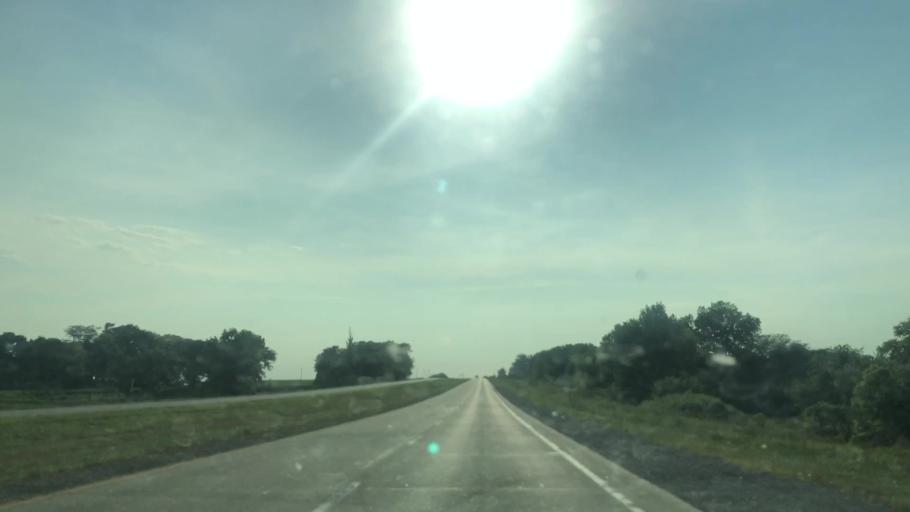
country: US
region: Iowa
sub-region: Story County
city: Nevada
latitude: 42.0077
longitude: -93.3839
